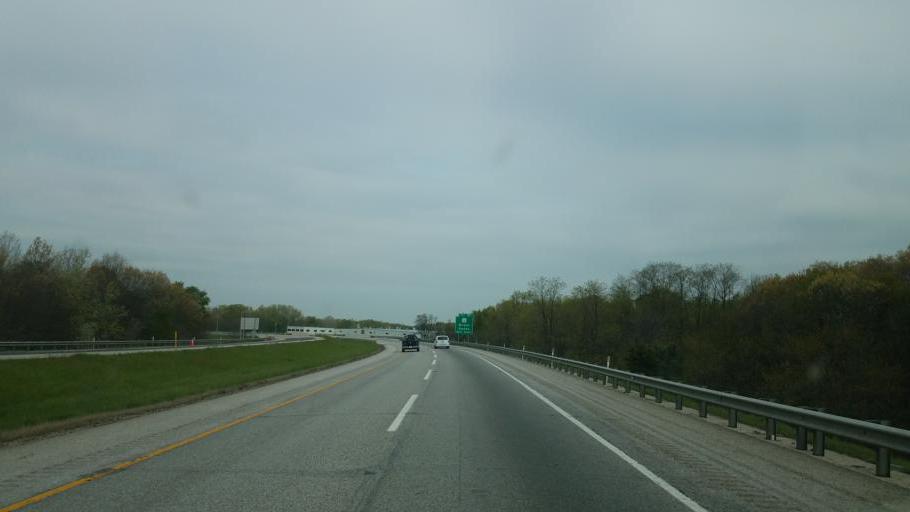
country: US
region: Indiana
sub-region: Elkhart County
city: Bristol
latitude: 41.7336
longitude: -85.7802
